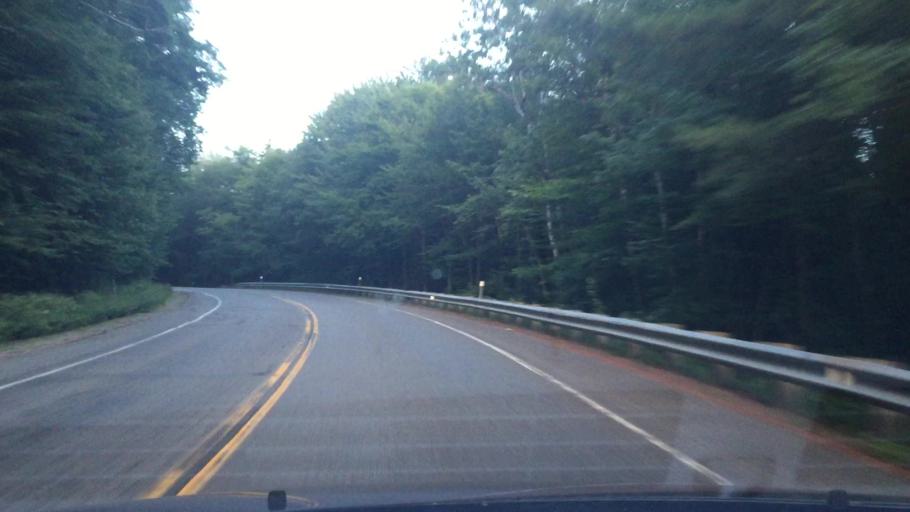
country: US
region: New Hampshire
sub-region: Grafton County
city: Woodstock
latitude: 44.0528
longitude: -71.5806
